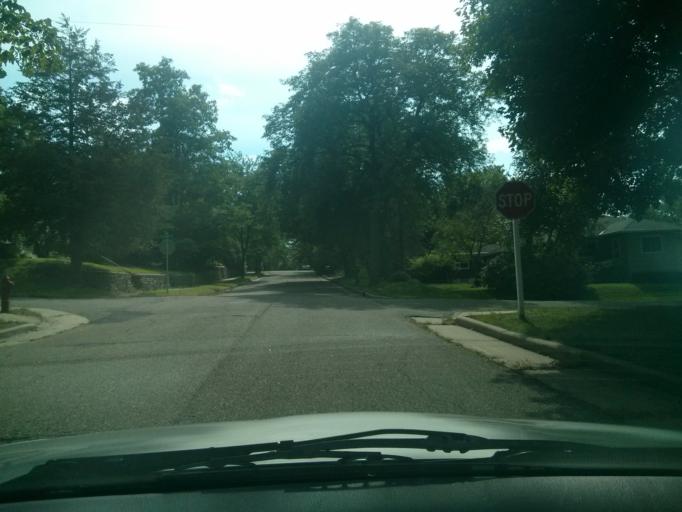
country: US
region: Wisconsin
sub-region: Saint Croix County
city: Hudson
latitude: 44.9806
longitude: -92.7452
